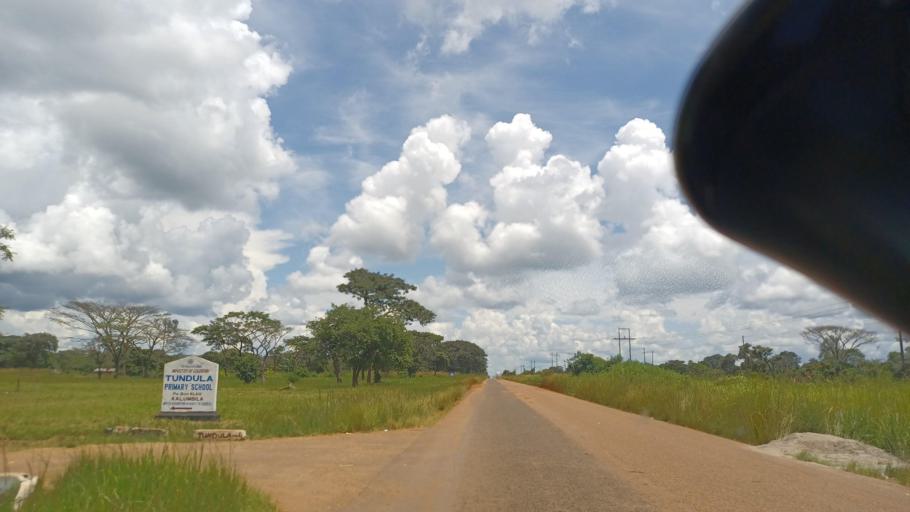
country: ZM
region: North-Western
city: Solwezi
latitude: -12.4884
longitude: 26.1921
